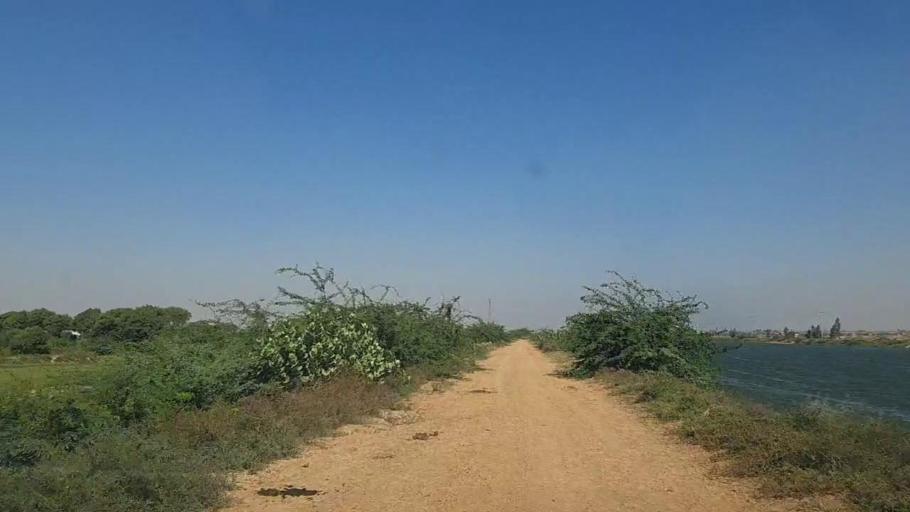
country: PK
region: Sindh
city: Thatta
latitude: 24.8178
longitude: 67.9893
